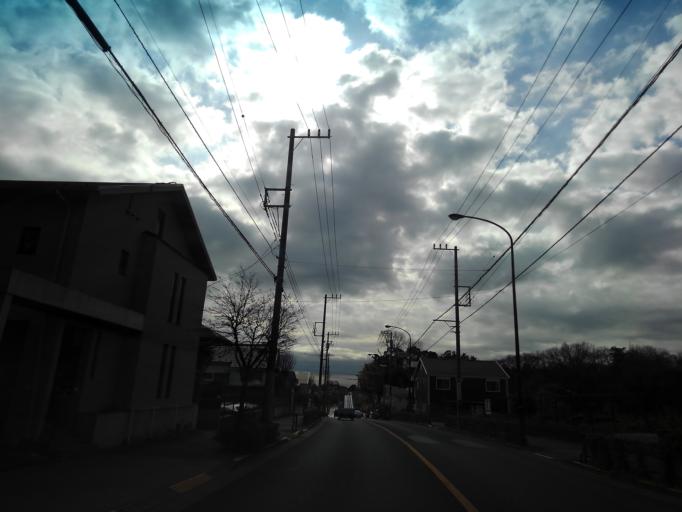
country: JP
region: Tokyo
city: Mitaka-shi
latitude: 35.6796
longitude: 139.5386
